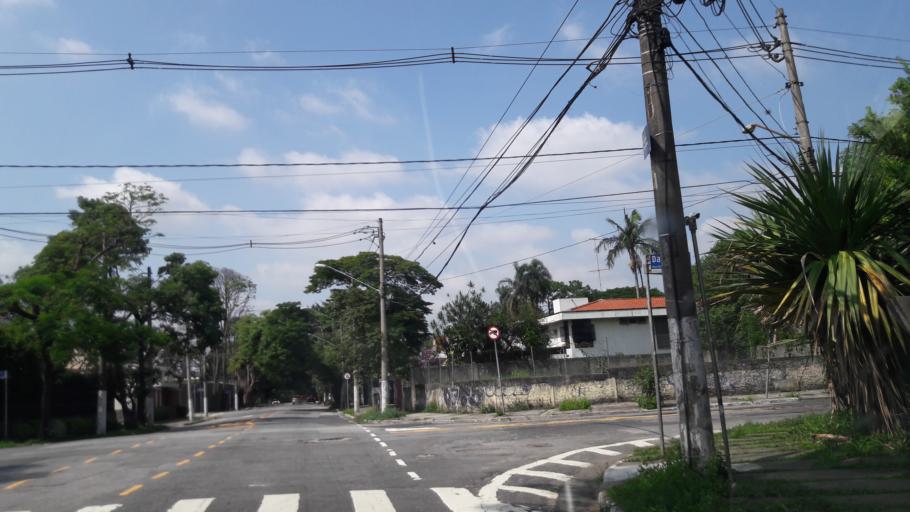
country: BR
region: Sao Paulo
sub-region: Sao Paulo
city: Sao Paulo
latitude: -23.5494
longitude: -46.7064
